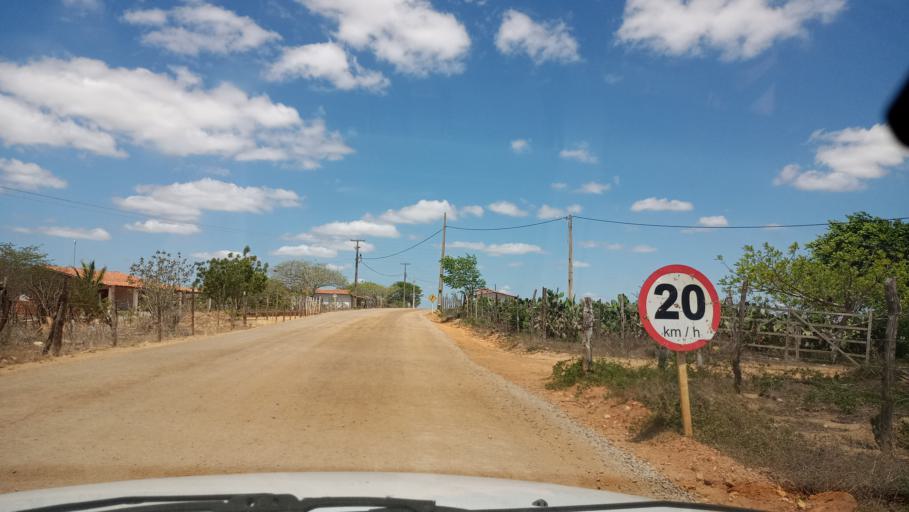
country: BR
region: Rio Grande do Norte
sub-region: Sao Paulo Do Potengi
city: Sao Paulo do Potengi
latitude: -5.7856
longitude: -35.9155
